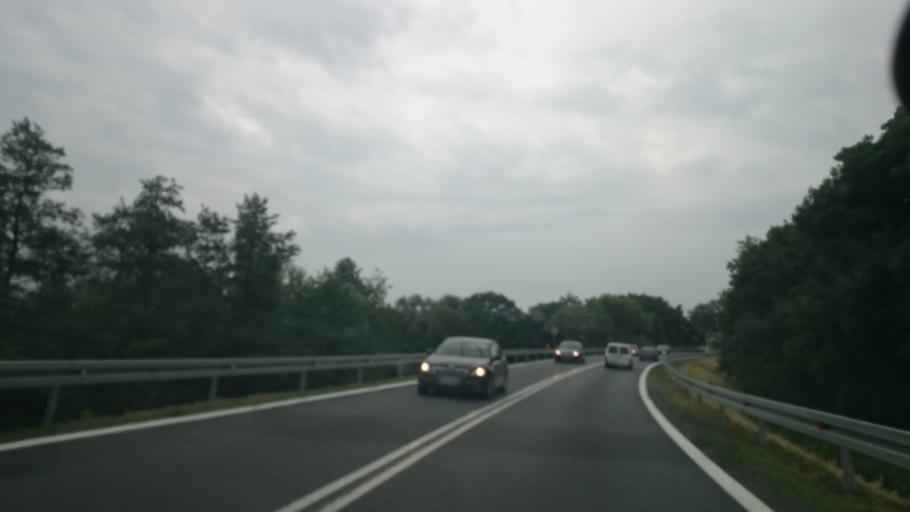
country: PL
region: Lower Silesian Voivodeship
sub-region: Powiat dzierzoniowski
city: Niemcza
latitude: 50.7340
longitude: 16.8373
